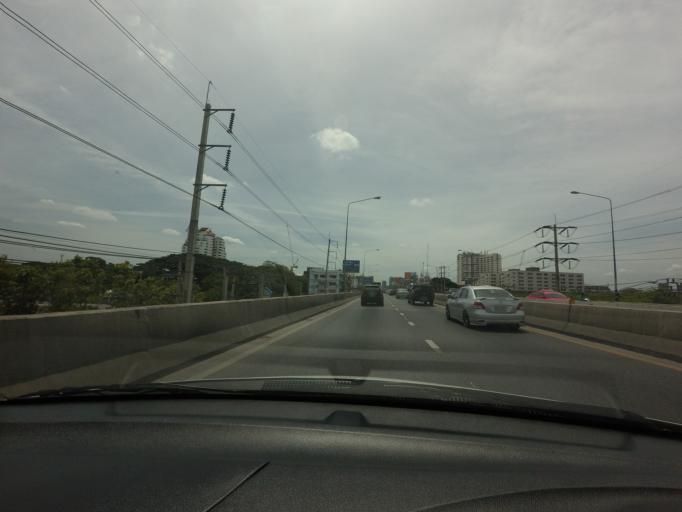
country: TH
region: Bangkok
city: Lak Si
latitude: 13.8915
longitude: 100.5650
